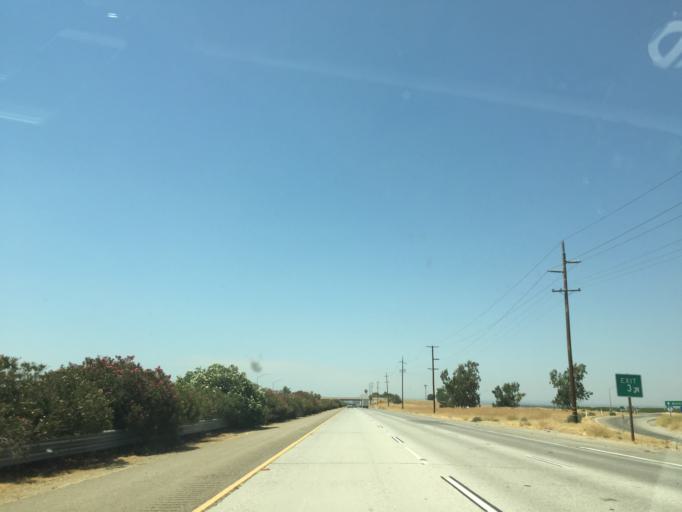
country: US
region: California
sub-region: Kern County
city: Weedpatch
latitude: 35.0521
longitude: -118.9660
